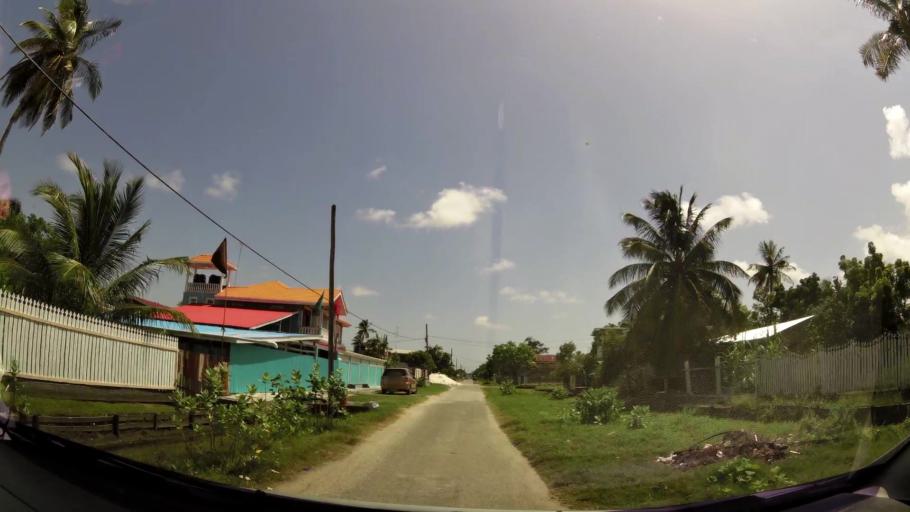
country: GY
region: Demerara-Mahaica
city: Mahaica Village
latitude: 6.7630
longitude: -58.0090
